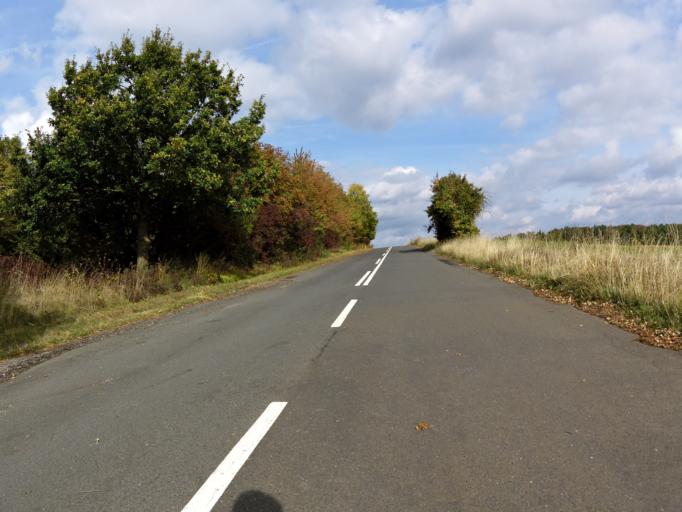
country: DE
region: Bavaria
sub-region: Regierungsbezirk Unterfranken
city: Reichenberg
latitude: 49.7340
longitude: 9.9344
